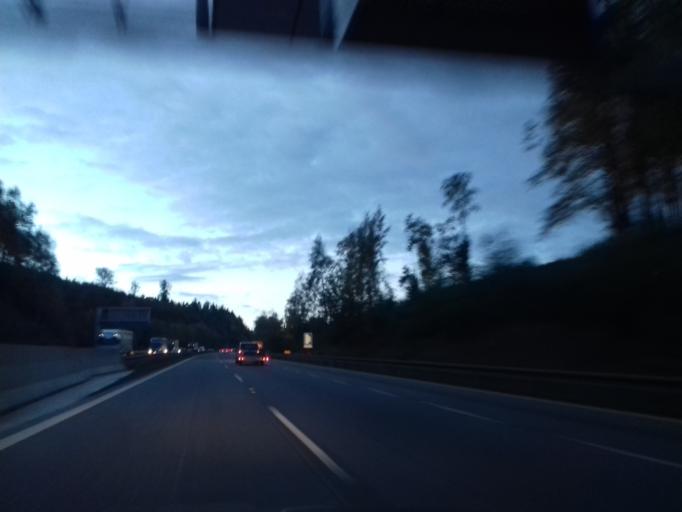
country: CZ
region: Central Bohemia
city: Divisov
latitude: 49.7870
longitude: 14.9280
